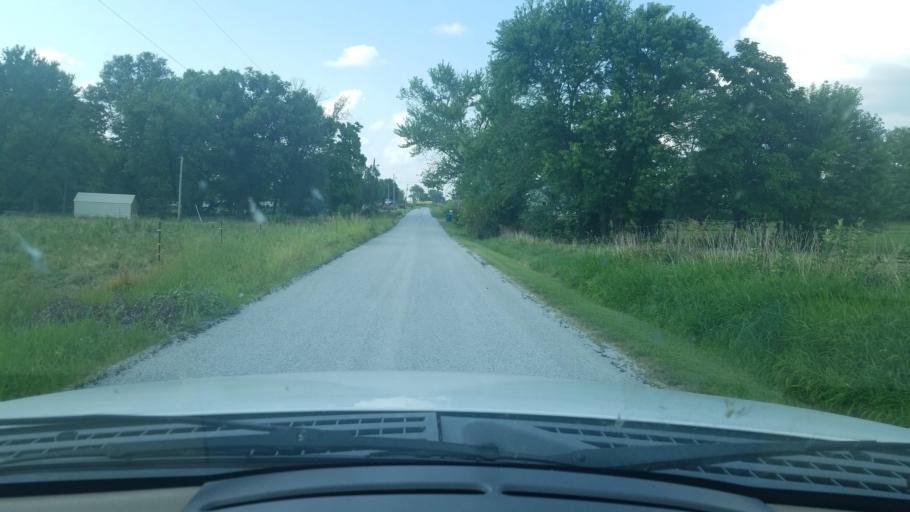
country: US
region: Illinois
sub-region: Saline County
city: Eldorado
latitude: 37.8296
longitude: -88.4385
